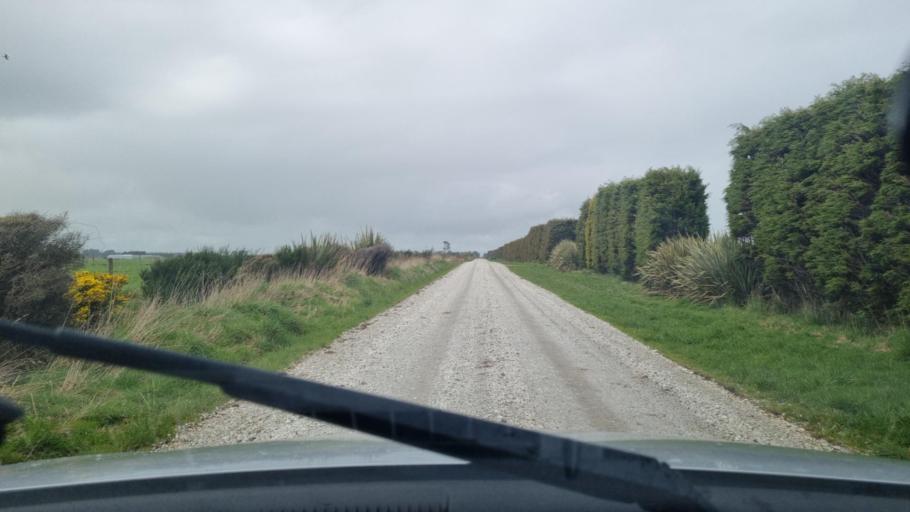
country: NZ
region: Southland
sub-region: Invercargill City
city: Invercargill
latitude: -46.5006
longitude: 168.4093
